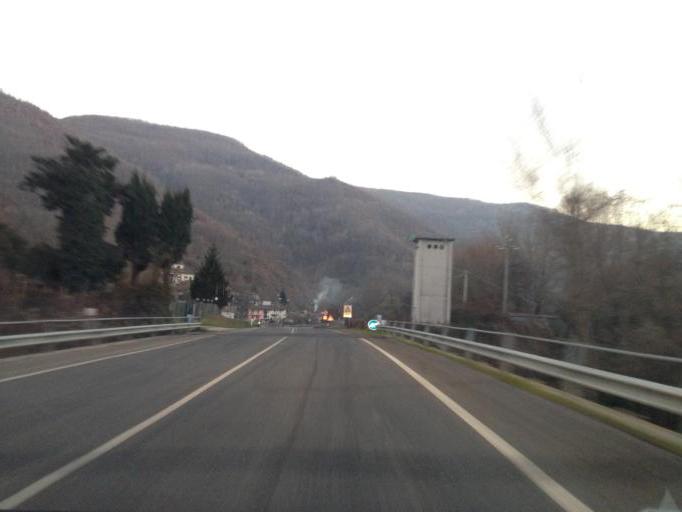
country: IT
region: Latium
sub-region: Provincia di Rieti
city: Accumoli
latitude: 42.7341
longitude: 13.2669
